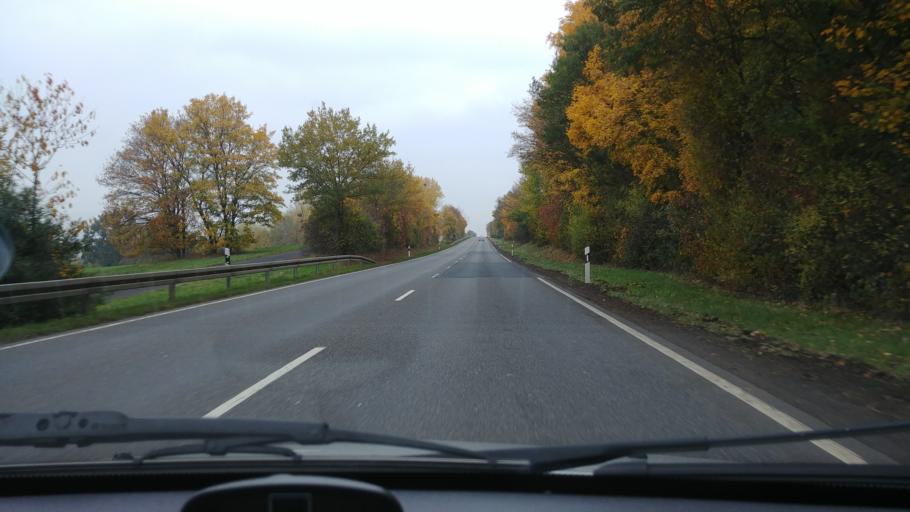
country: DE
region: Hesse
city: Waldbrunn
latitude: 50.4830
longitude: 8.0602
